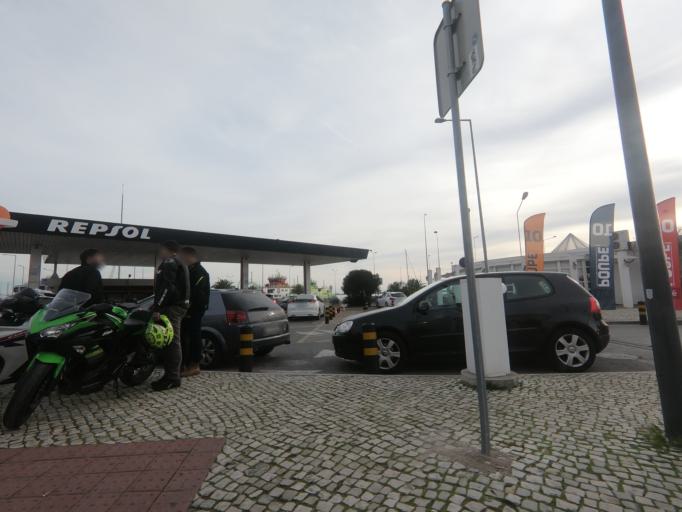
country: PT
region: Setubal
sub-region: Setubal
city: Setubal
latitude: 38.5227
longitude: -8.8863
